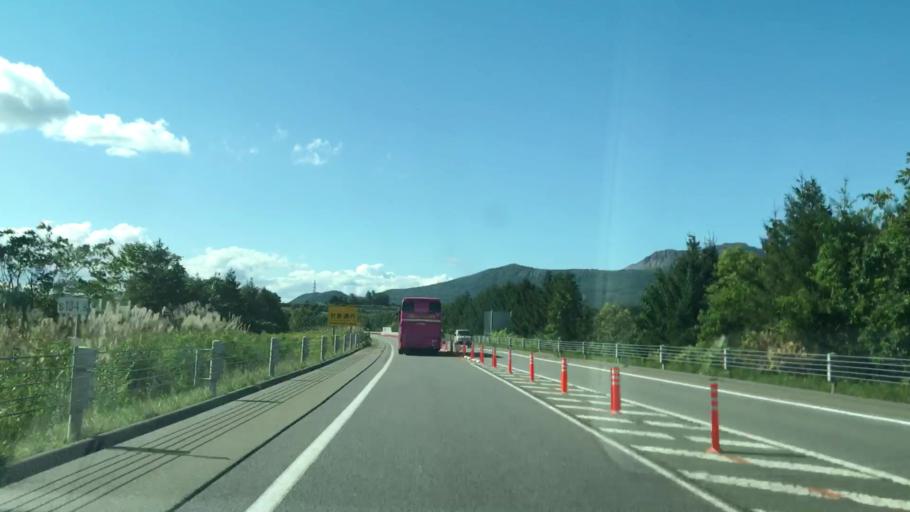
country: JP
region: Hokkaido
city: Date
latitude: 42.4928
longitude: 140.8764
